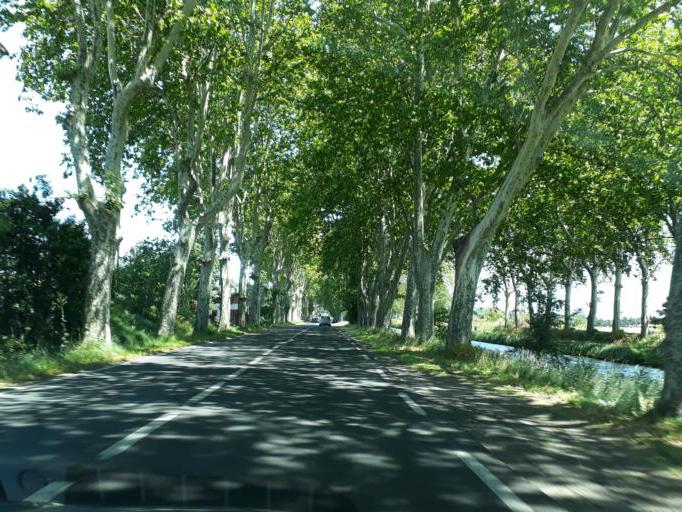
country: FR
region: Languedoc-Roussillon
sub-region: Departement de l'Herault
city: Villeneuve-les-Beziers
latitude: 43.3236
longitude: 3.2522
